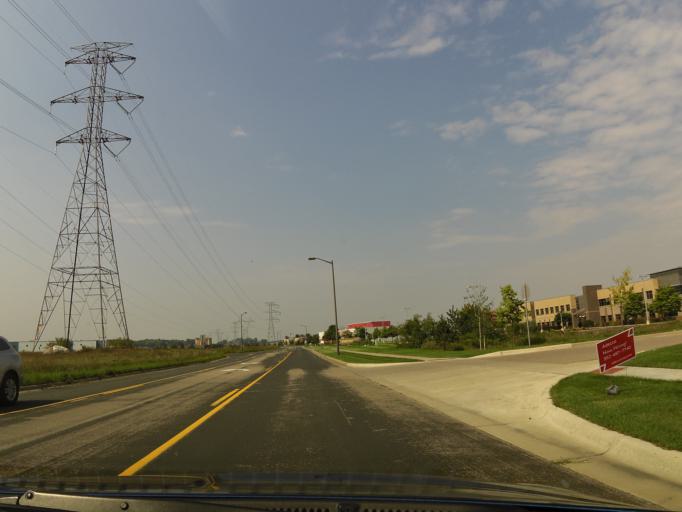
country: US
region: Minnesota
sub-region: Scott County
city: Shakopee
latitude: 44.7809
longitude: -93.4586
